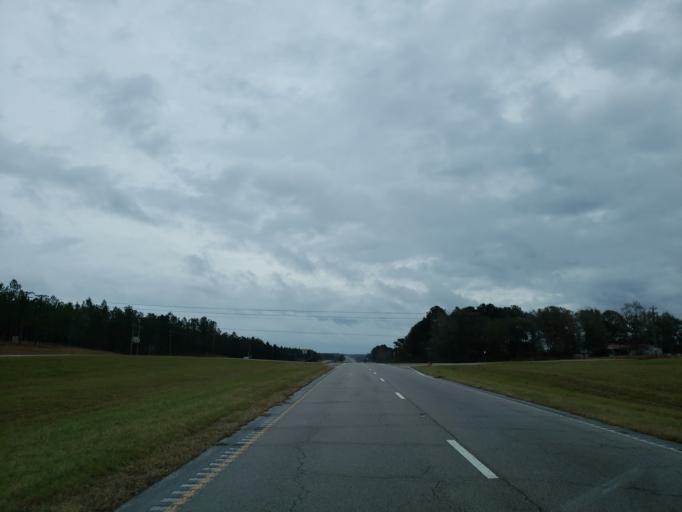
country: US
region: Mississippi
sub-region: Wayne County
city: Waynesboro
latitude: 31.6966
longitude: -88.8738
